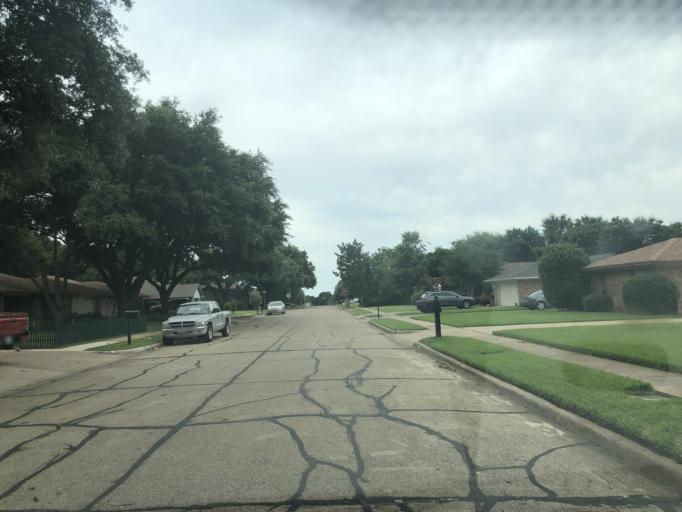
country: US
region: Texas
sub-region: Dallas County
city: Irving
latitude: 32.7985
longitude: -96.9854
